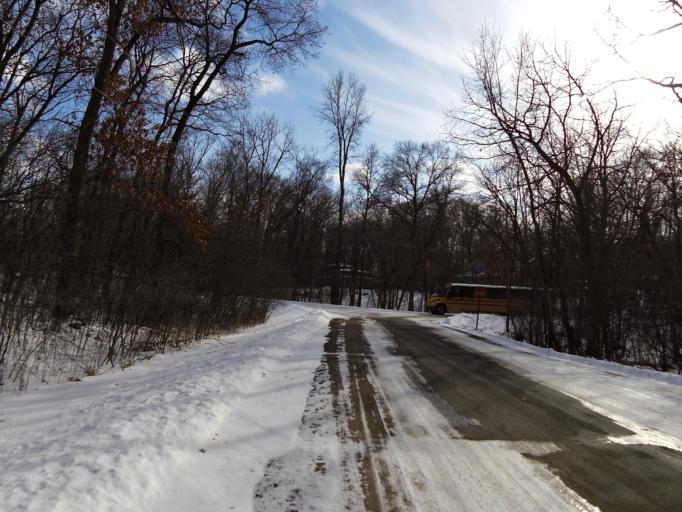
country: US
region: Minnesota
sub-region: Washington County
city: Lake Elmo
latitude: 44.9677
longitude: -92.8348
